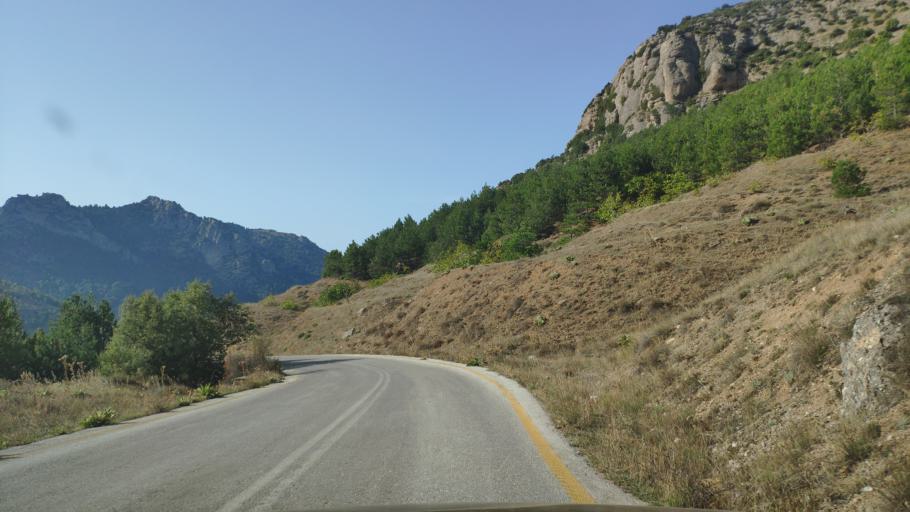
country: GR
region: West Greece
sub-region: Nomos Achaias
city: Aiyira
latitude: 38.0435
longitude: 22.3906
